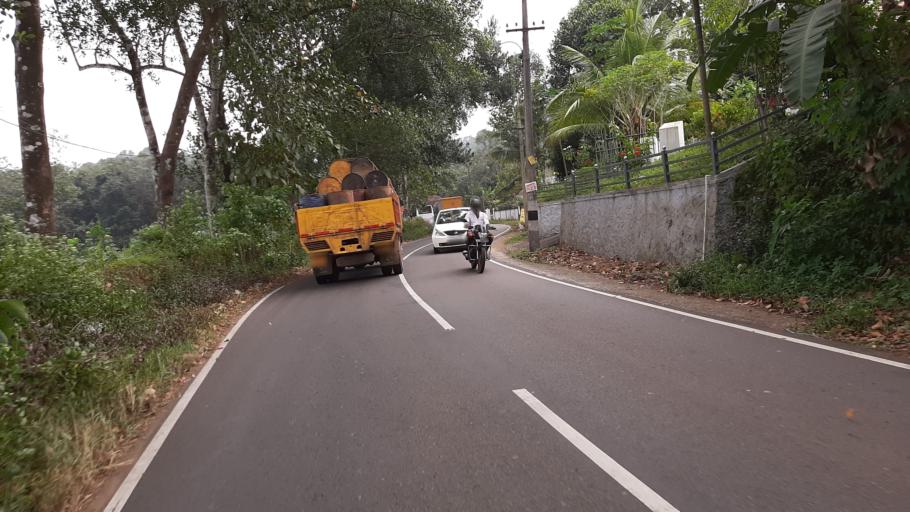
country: IN
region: Kerala
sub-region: Pattanamtitta
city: Pathanamthitta
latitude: 9.4701
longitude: 76.8694
